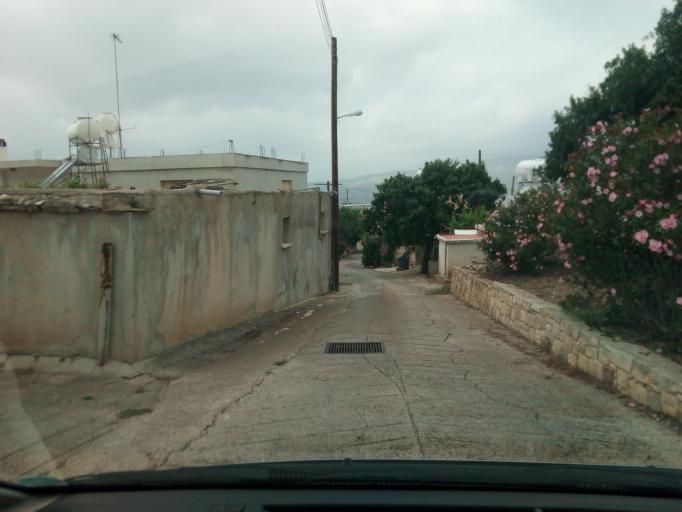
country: CY
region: Limassol
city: Pachna
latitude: 34.8120
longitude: 32.6506
